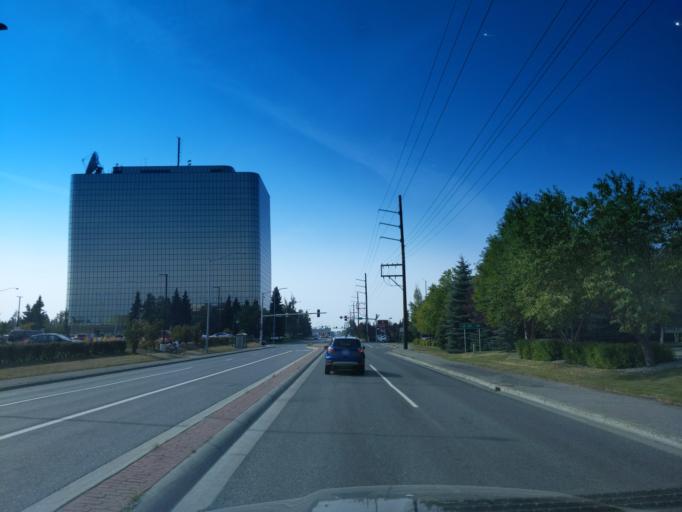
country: US
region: Alaska
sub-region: Anchorage Municipality
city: Anchorage
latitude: 61.1881
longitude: -149.8807
